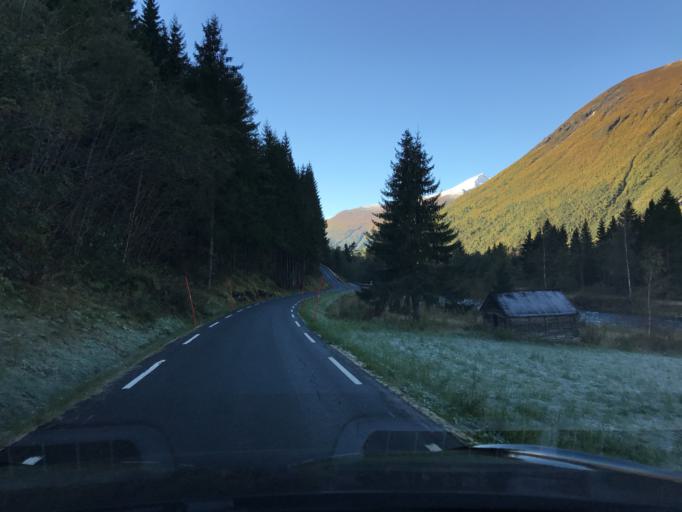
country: NO
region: More og Romsdal
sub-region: Norddal
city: Valldal
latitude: 62.3293
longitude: 7.3469
